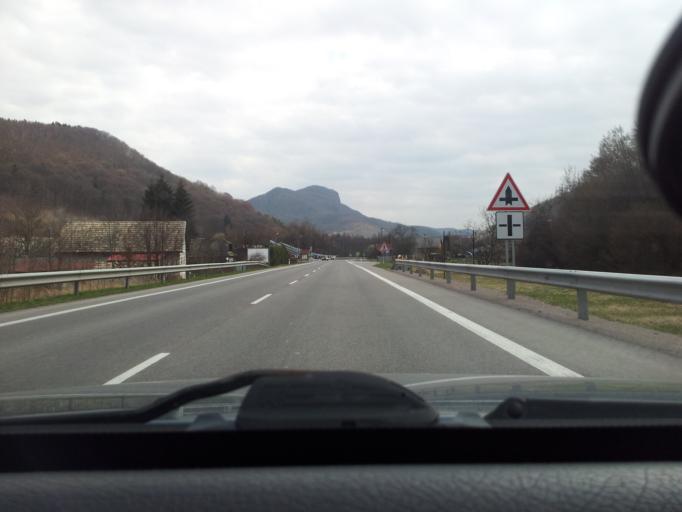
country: SK
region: Banskobystricky
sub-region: Okres Ziar nad Hronom
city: Kremnica
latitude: 48.6655
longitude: 18.9112
